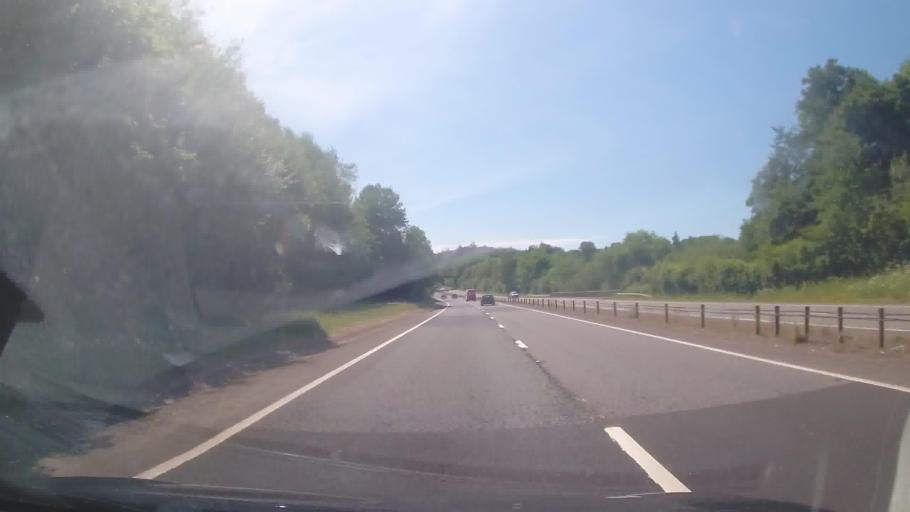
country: GB
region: England
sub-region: Devon
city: Ottery St Mary
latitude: 50.7693
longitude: -3.2941
